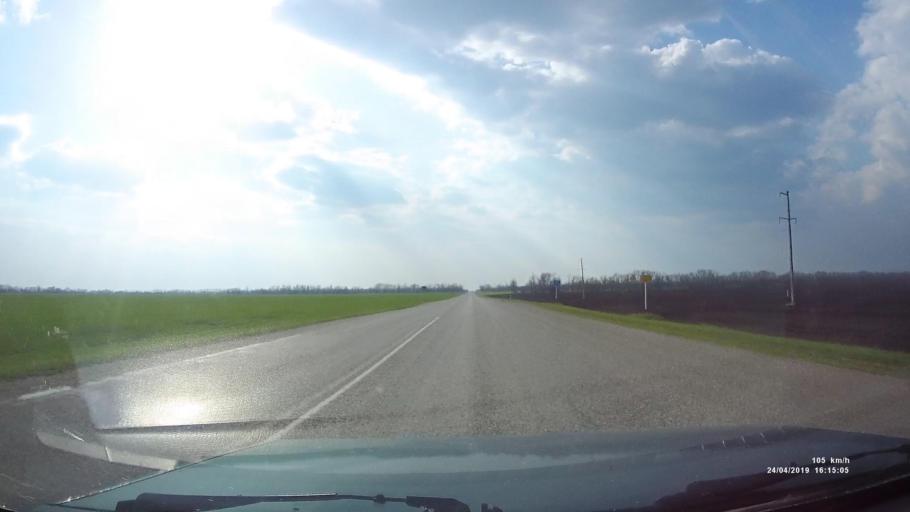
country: RU
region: Rostov
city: Sovetskoye
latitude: 46.7555
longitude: 42.1889
